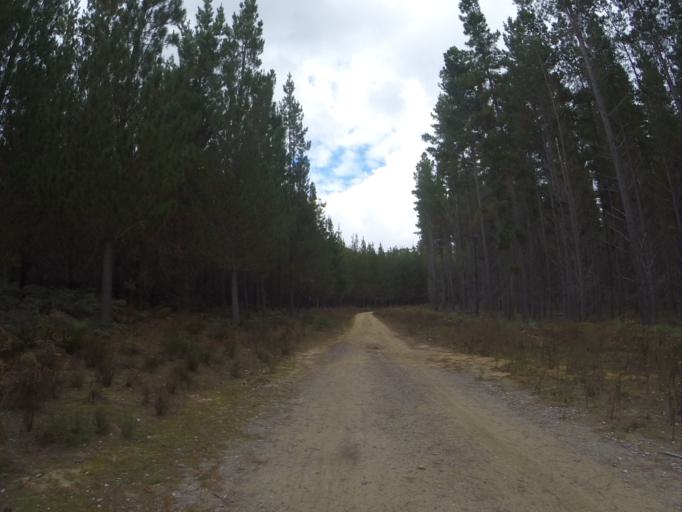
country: AU
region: New South Wales
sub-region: Wingecarribee
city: Moss Vale
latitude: -34.5192
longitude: 150.2474
